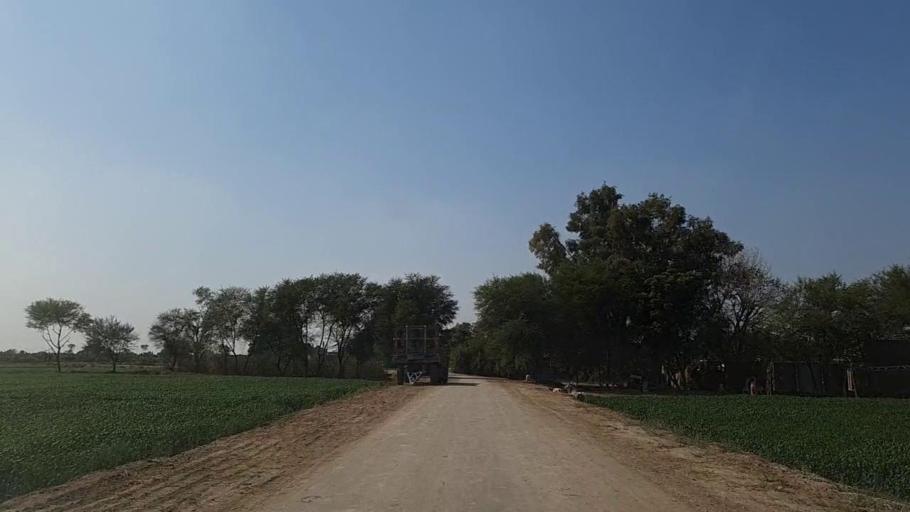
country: PK
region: Sindh
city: Daur
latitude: 26.4914
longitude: 68.2536
